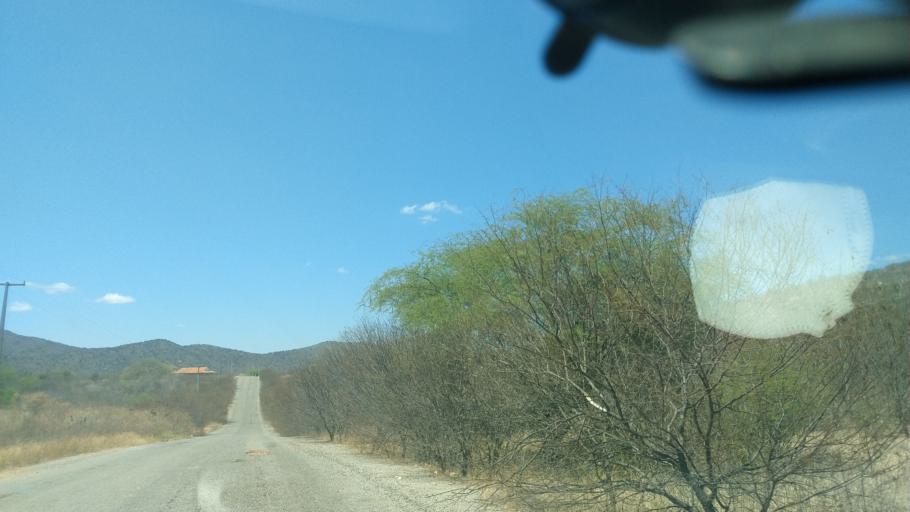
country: BR
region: Rio Grande do Norte
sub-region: Sao Tome
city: Sao Tome
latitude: -5.9755
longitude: -36.1423
